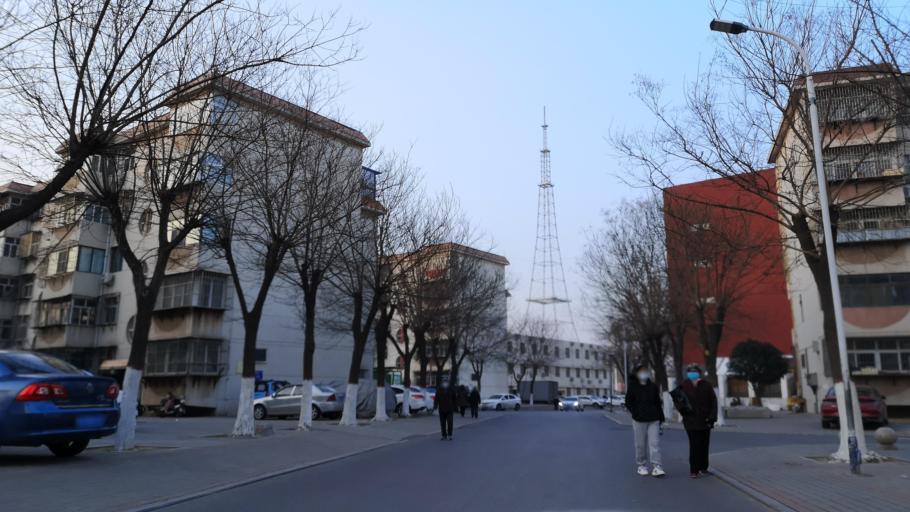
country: CN
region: Henan Sheng
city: Zhongyuanlu
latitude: 35.7697
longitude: 115.0792
